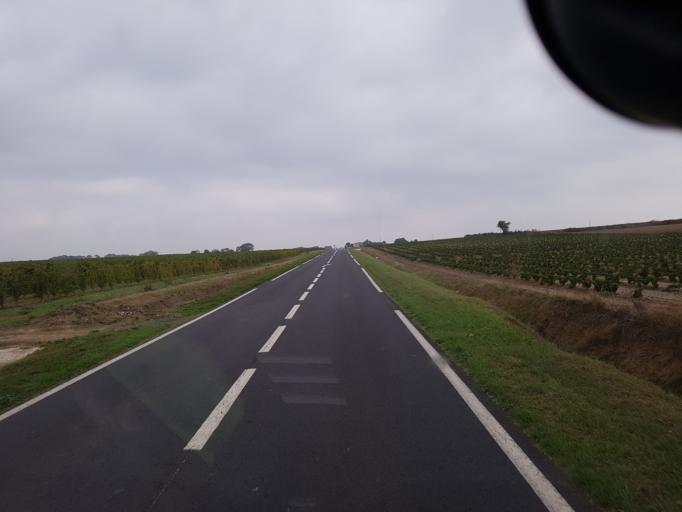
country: FR
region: Languedoc-Roussillon
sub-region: Departement de l'Herault
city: Pinet
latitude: 43.4085
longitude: 3.5423
